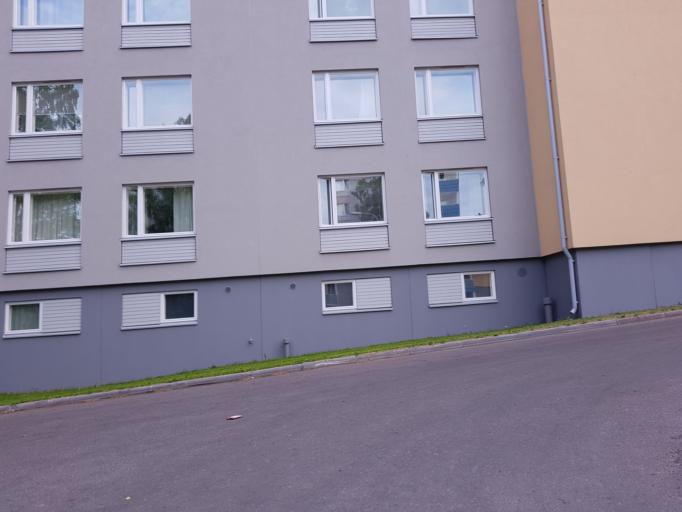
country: FI
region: Uusimaa
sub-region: Helsinki
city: Teekkarikylae
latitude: 60.2360
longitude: 24.8766
